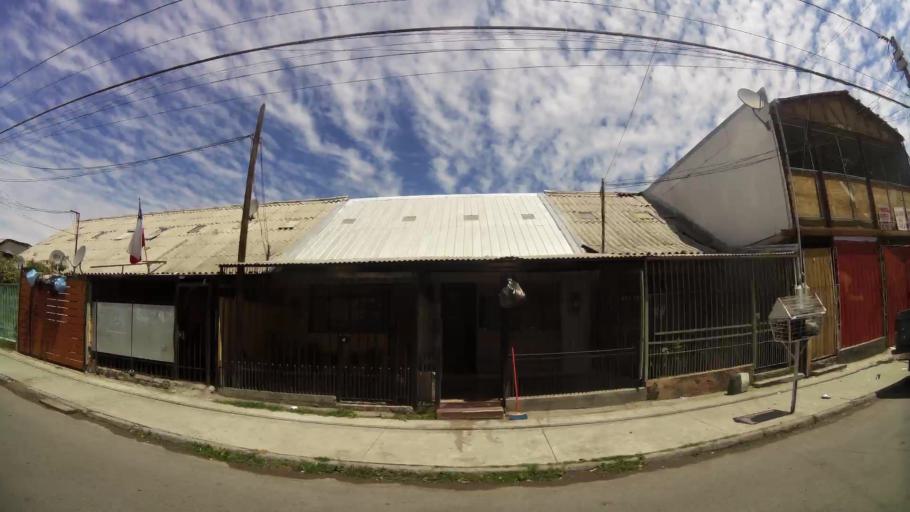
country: CL
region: Santiago Metropolitan
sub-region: Provincia de Santiago
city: La Pintana
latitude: -33.5500
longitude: -70.6420
